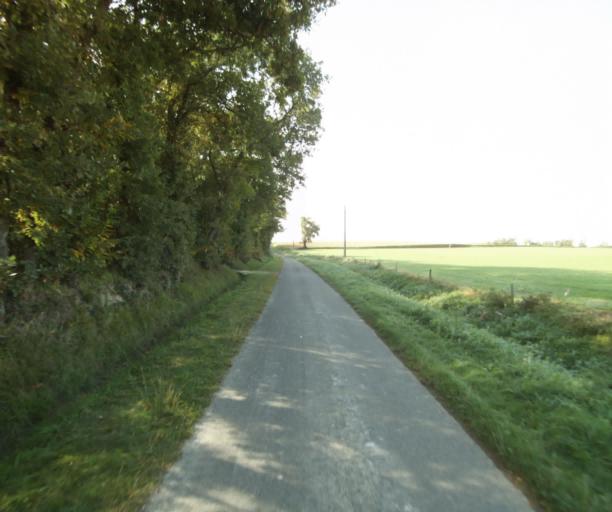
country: FR
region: Midi-Pyrenees
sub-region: Departement du Gers
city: Eauze
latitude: 43.9188
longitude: 0.1215
